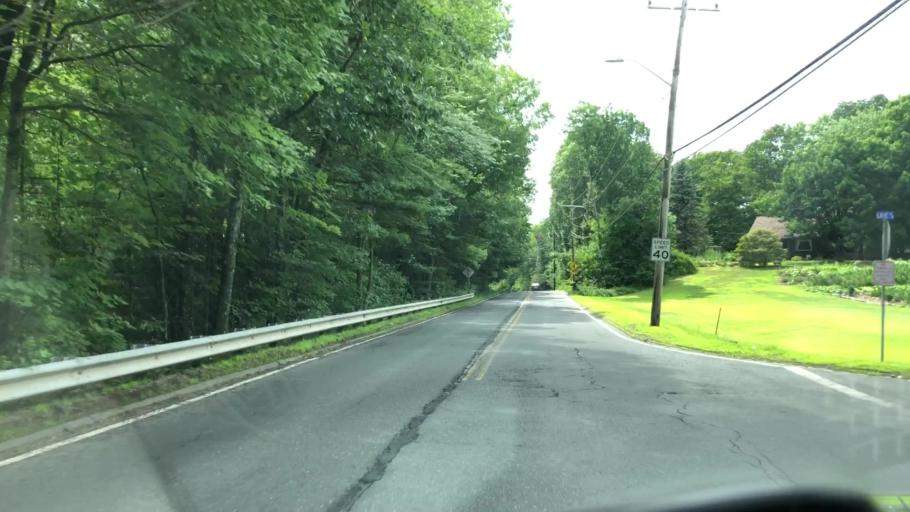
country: US
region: Massachusetts
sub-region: Hampden County
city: Holyoke
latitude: 42.2169
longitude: -72.6640
